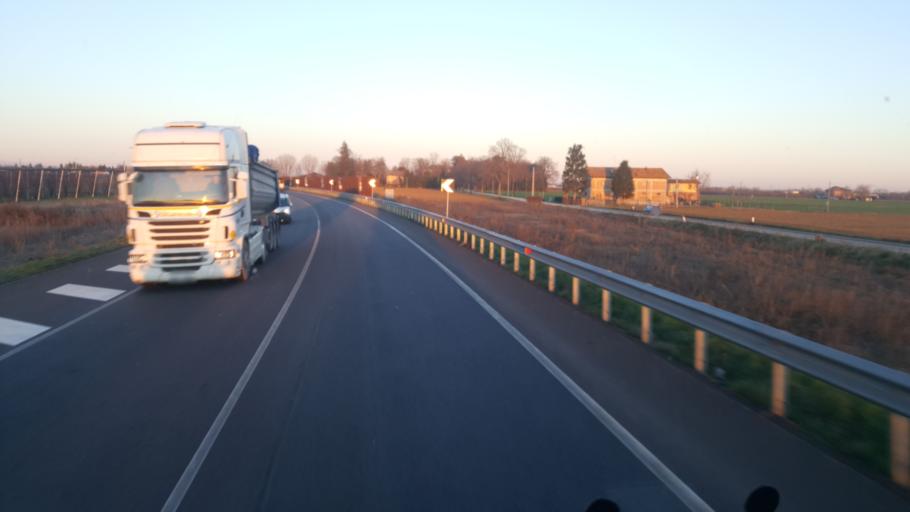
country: IT
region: Emilia-Romagna
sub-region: Provincia di Bologna
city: Crespellano
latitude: 44.5220
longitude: 11.1347
